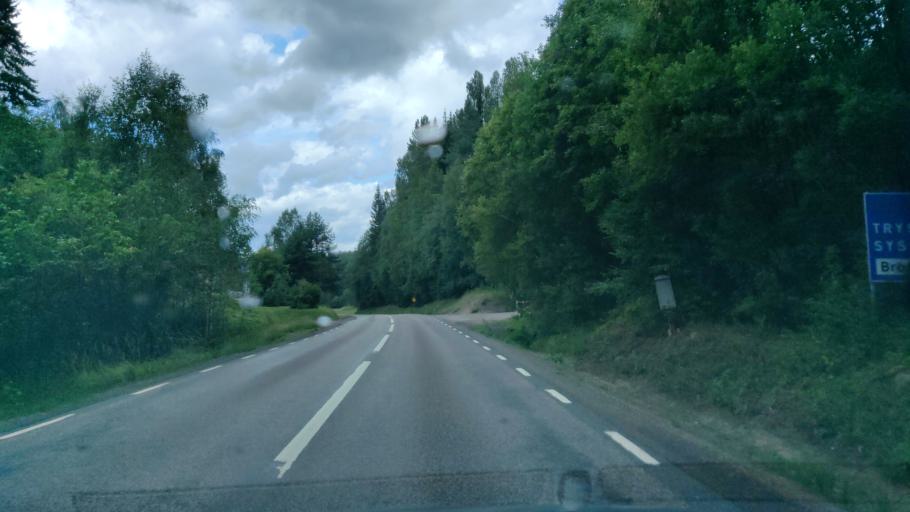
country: SE
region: Vaermland
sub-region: Torsby Kommun
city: Torsby
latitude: 60.6240
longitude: 13.0312
